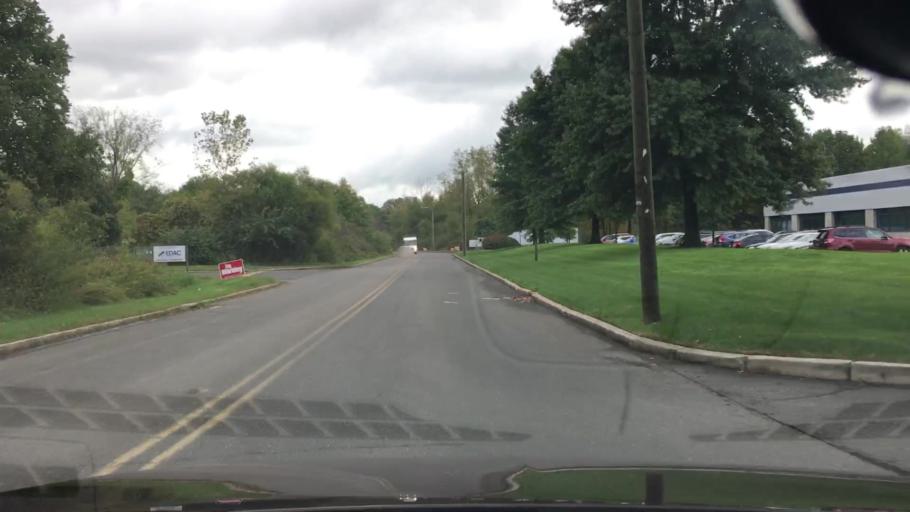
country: US
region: Connecticut
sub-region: New Haven County
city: Cheshire Village
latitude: 41.5497
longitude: -72.9234
